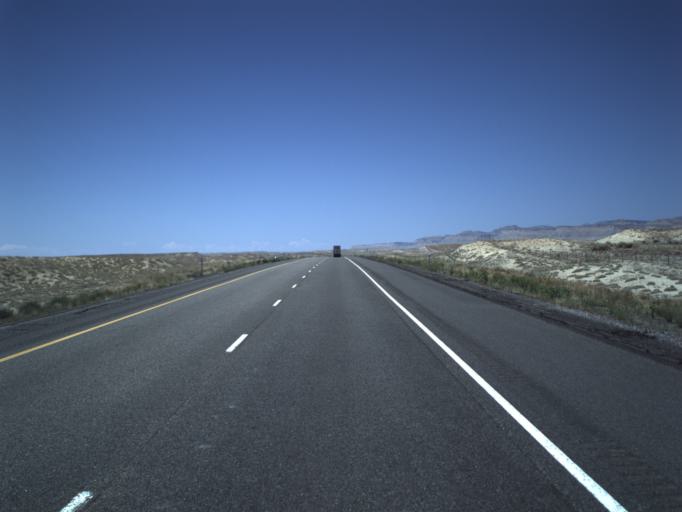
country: US
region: Utah
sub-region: Grand County
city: Moab
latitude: 38.9387
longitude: -109.4898
